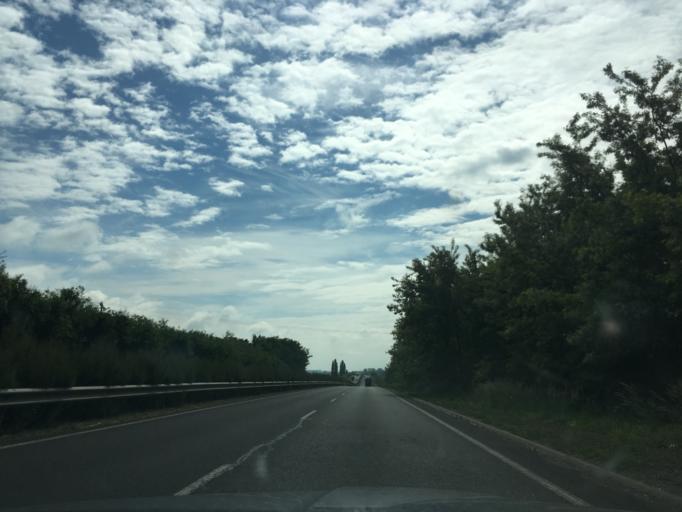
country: HU
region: Borsod-Abauj-Zemplen
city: Felsozsolca
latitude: 48.1093
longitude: 20.8873
